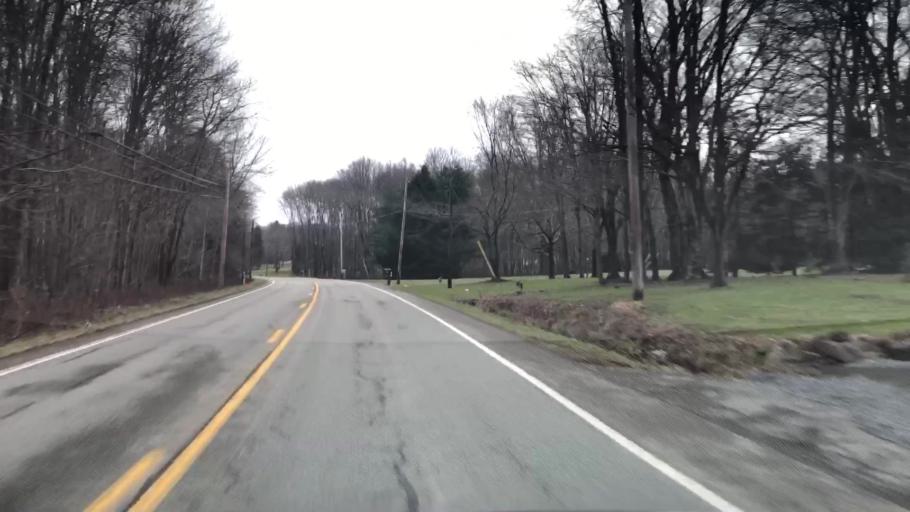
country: US
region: Pennsylvania
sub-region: Mercer County
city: Grove City
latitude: 41.1260
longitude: -80.0699
